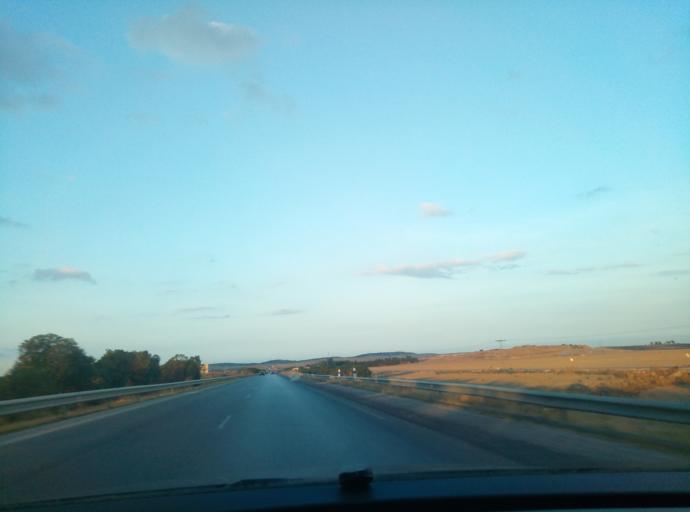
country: TN
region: Tunis
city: Oued Lill
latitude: 36.7347
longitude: 10.0179
